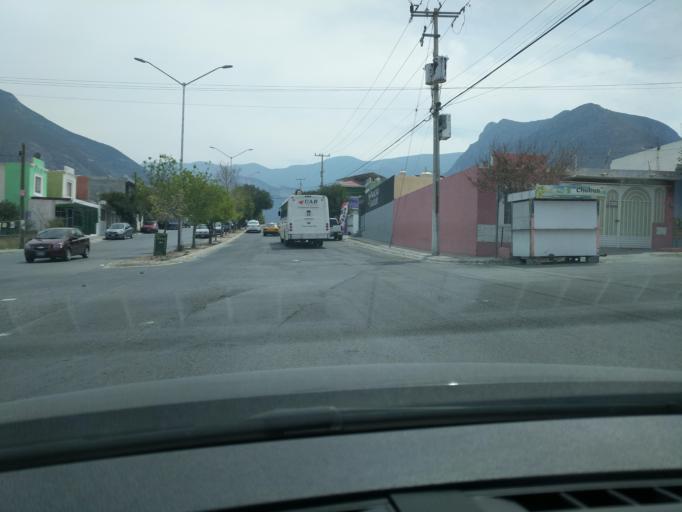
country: MX
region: Coahuila
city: Saltillo
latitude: 25.3512
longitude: -101.0122
